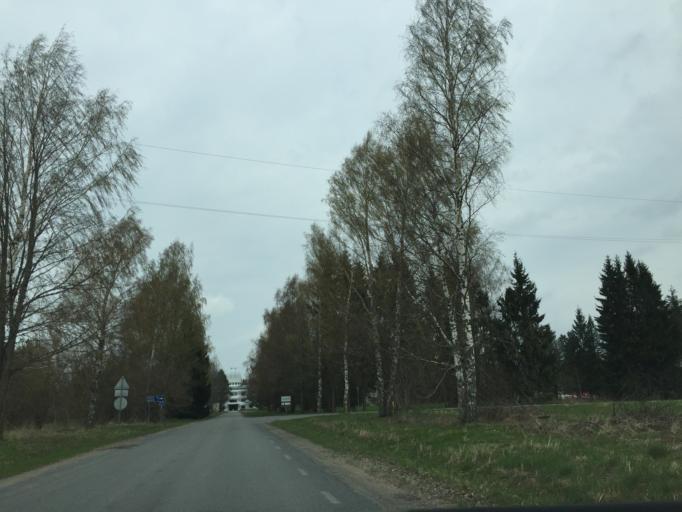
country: EE
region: Tartu
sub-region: Elva linn
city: Elva
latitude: 58.2632
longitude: 26.4690
